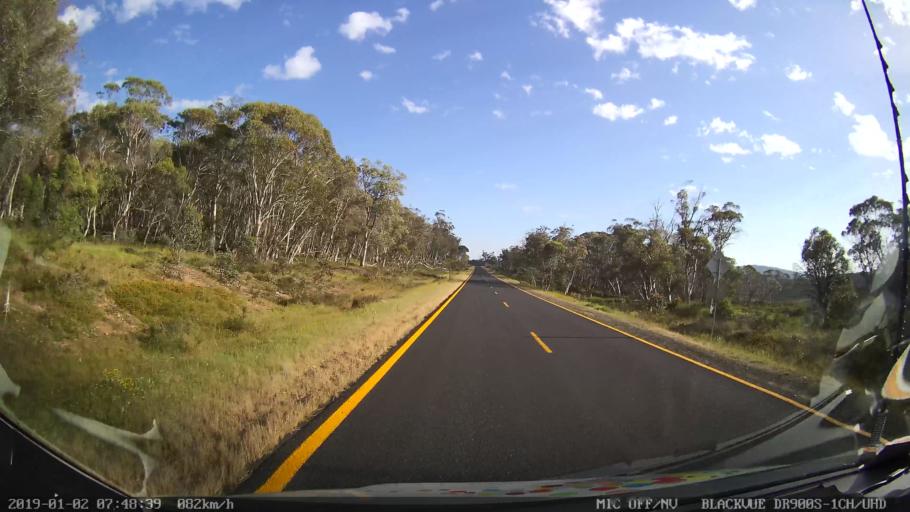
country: AU
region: New South Wales
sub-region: Tumut Shire
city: Tumut
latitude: -35.7506
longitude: 148.5190
